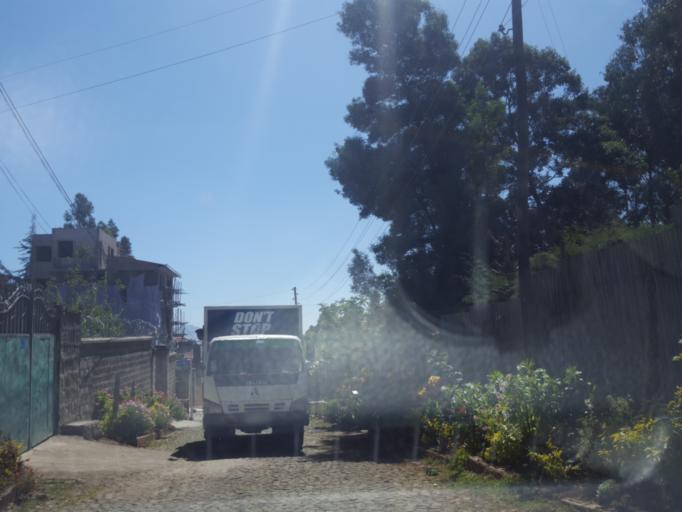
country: ET
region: Adis Abeba
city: Addis Ababa
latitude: 9.0568
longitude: 38.7448
